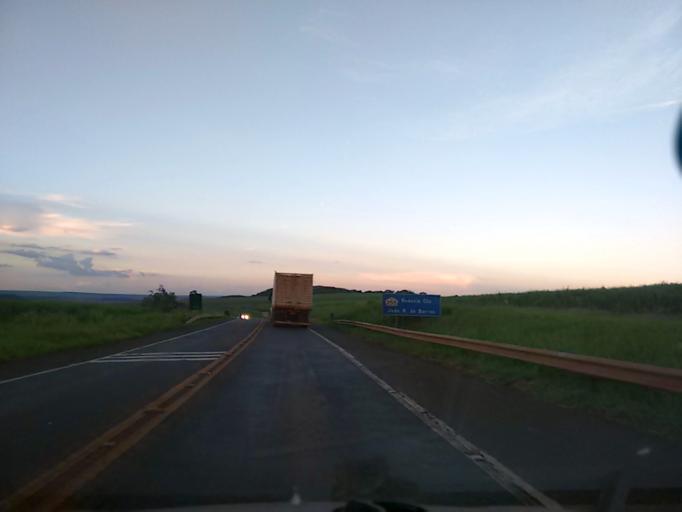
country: BR
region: Sao Paulo
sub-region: Boa Esperanca Do Sul
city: Boa Esperanca do Sul
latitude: -22.1186
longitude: -48.4559
